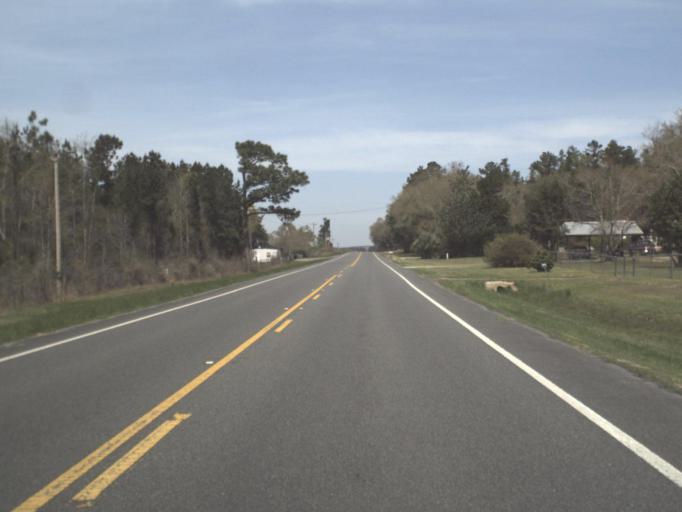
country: US
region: Florida
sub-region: Walton County
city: DeFuniak Springs
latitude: 30.7567
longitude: -85.9590
